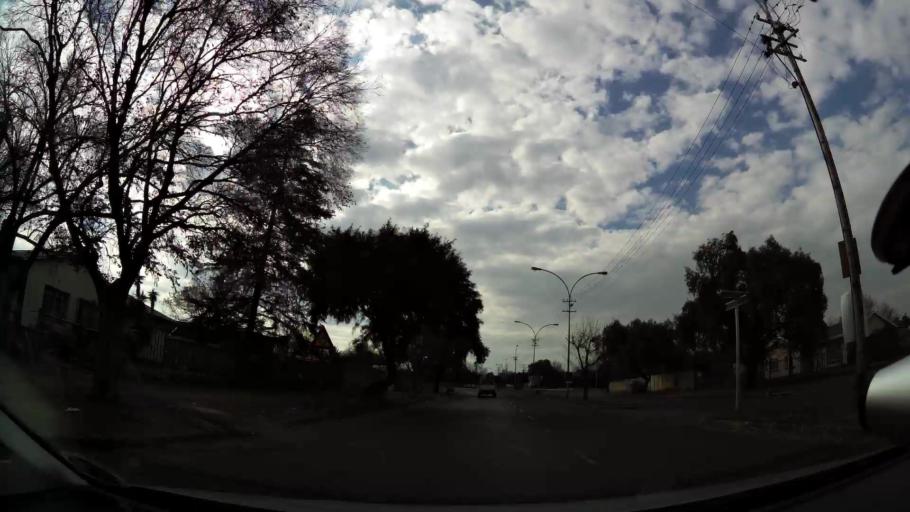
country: ZA
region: Orange Free State
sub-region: Mangaung Metropolitan Municipality
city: Bloemfontein
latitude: -29.0811
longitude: 26.2445
